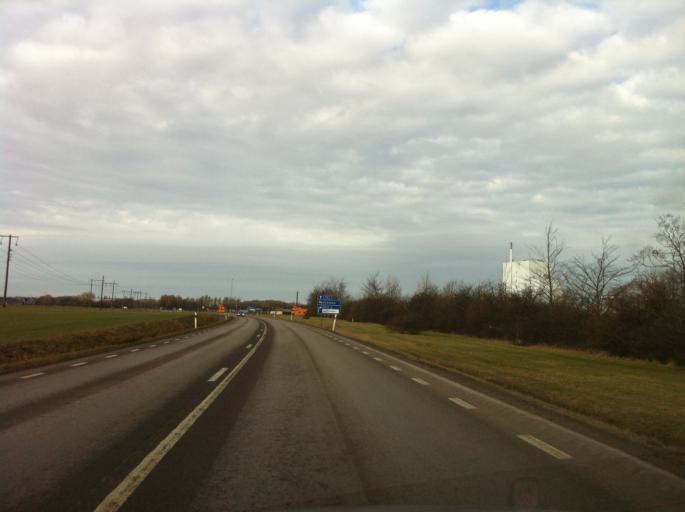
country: SE
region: Skane
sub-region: Bjuvs Kommun
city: Bjuv
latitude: 56.0704
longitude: 12.9372
